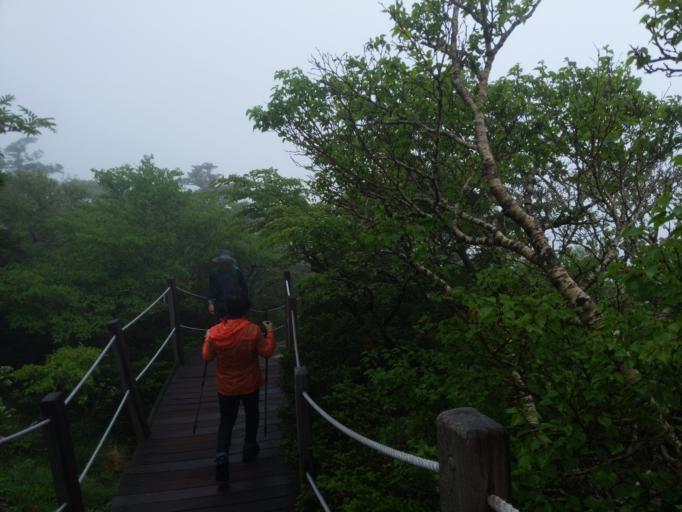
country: KR
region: Jeju-do
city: Seogwipo
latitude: 33.3632
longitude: 126.5409
